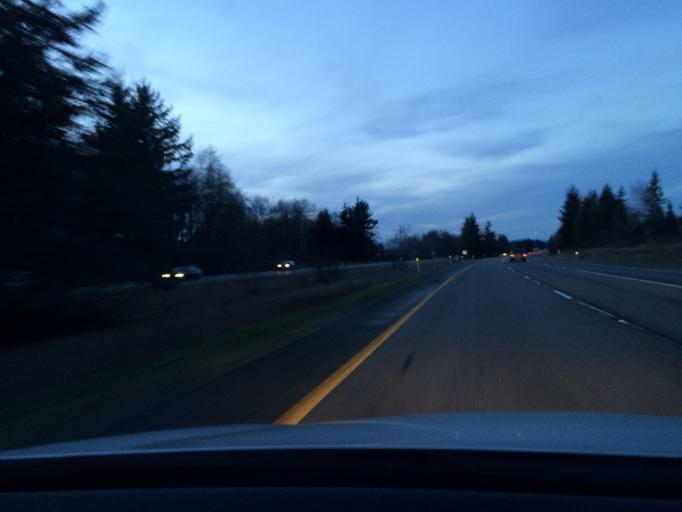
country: US
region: Washington
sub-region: Whatcom County
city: Ferndale
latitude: 48.9112
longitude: -122.6261
